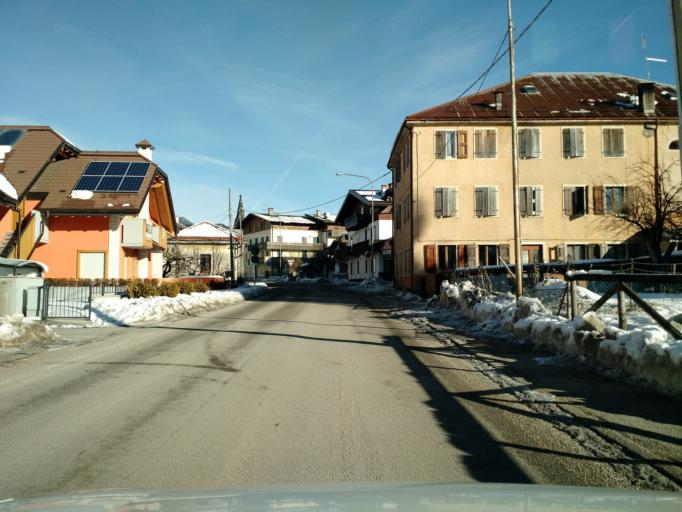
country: IT
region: Veneto
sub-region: Provincia di Vicenza
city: Canove di Roana
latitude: 45.8614
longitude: 11.4725
